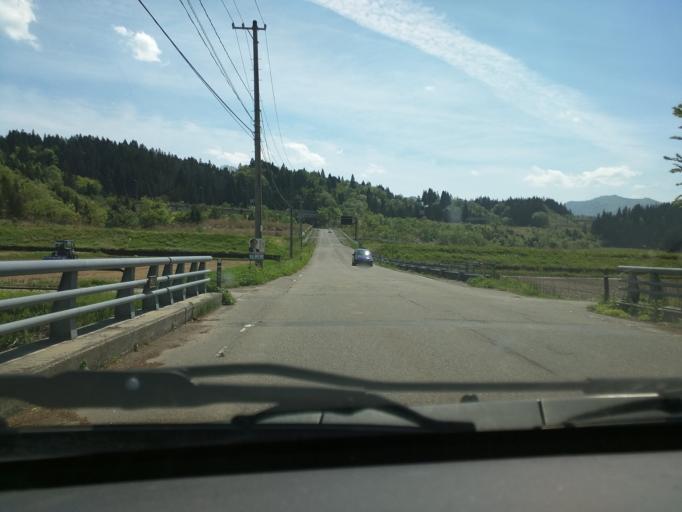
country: JP
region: Fukushima
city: Kitakata
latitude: 37.5812
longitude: 139.6445
